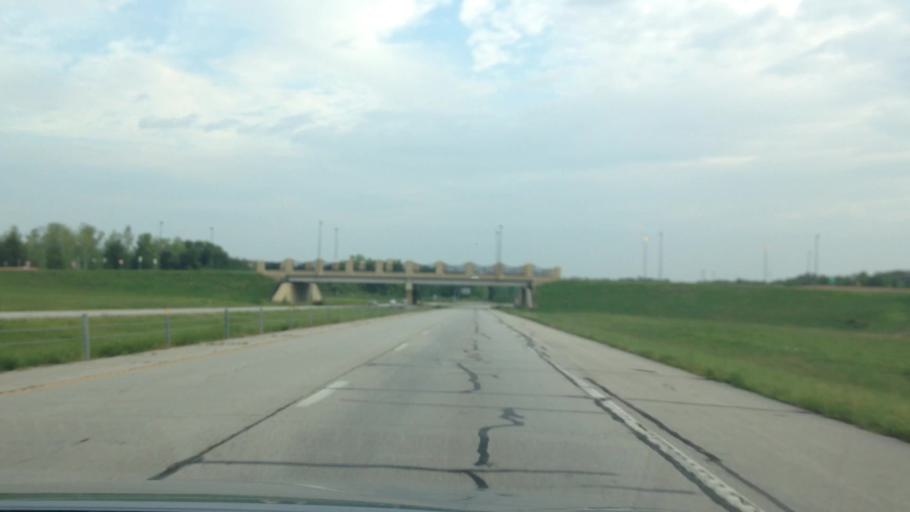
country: US
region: Missouri
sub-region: Clay County
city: Gladstone
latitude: 39.2720
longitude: -94.5850
